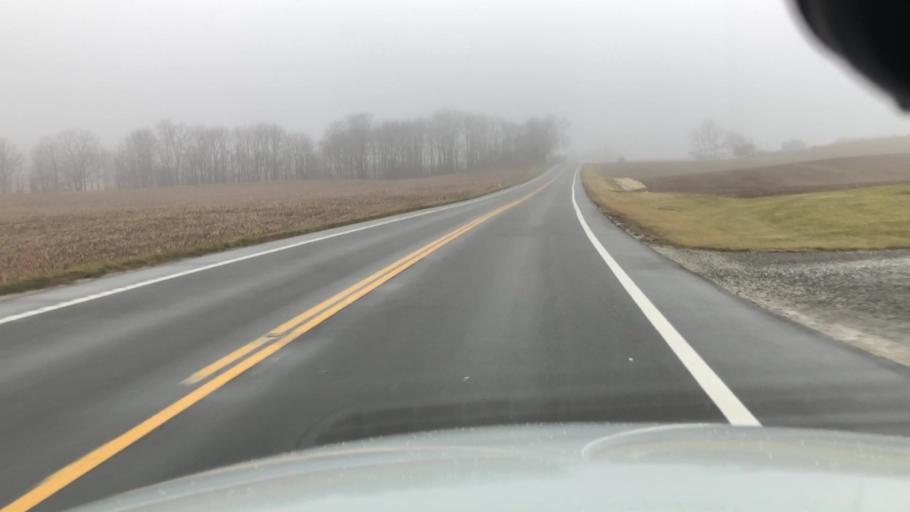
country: US
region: Ohio
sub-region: Logan County
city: Lakeview
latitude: 40.6065
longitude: -83.8873
